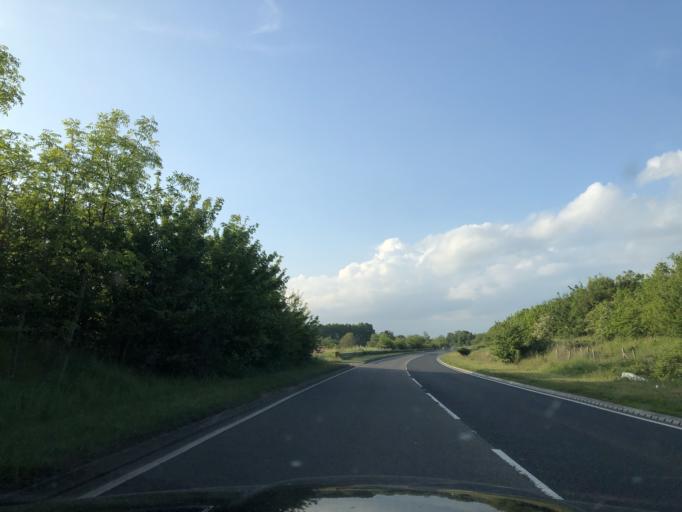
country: GB
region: England
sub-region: Warwickshire
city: Warwick
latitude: 52.2432
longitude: -1.6111
